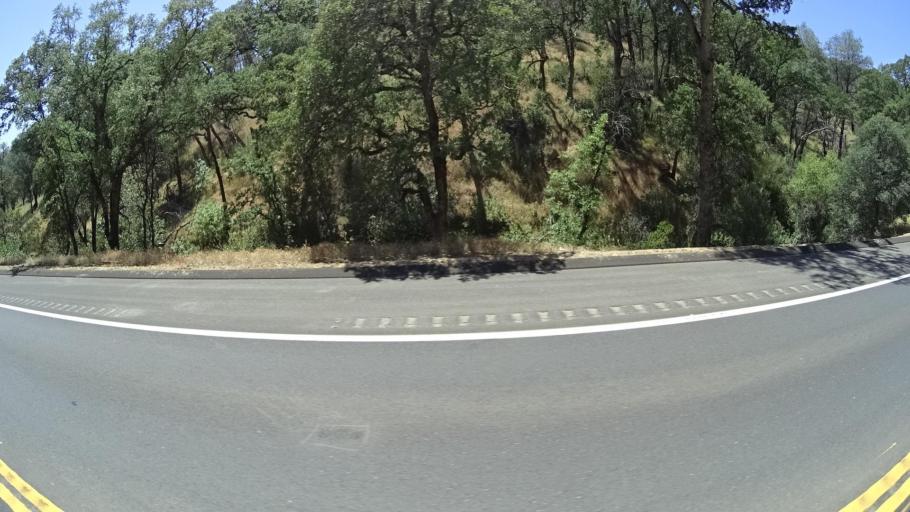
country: US
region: California
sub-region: Lake County
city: Hidden Valley Lake
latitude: 38.8308
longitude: -122.5861
